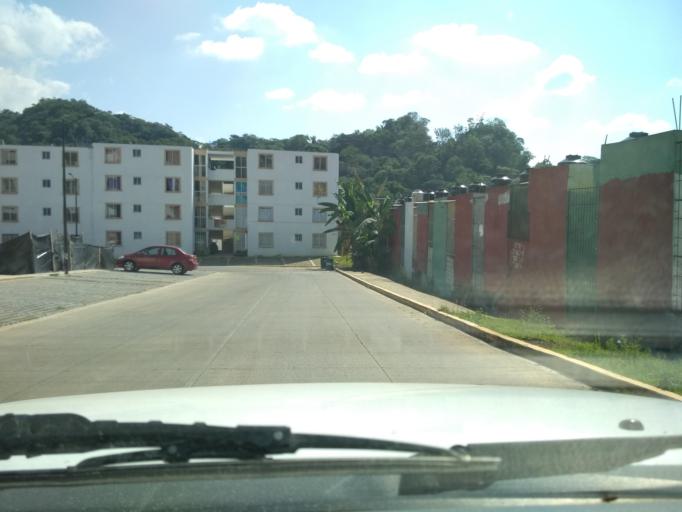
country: MX
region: Veracruz
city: Cordoba
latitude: 18.8726
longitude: -96.9077
